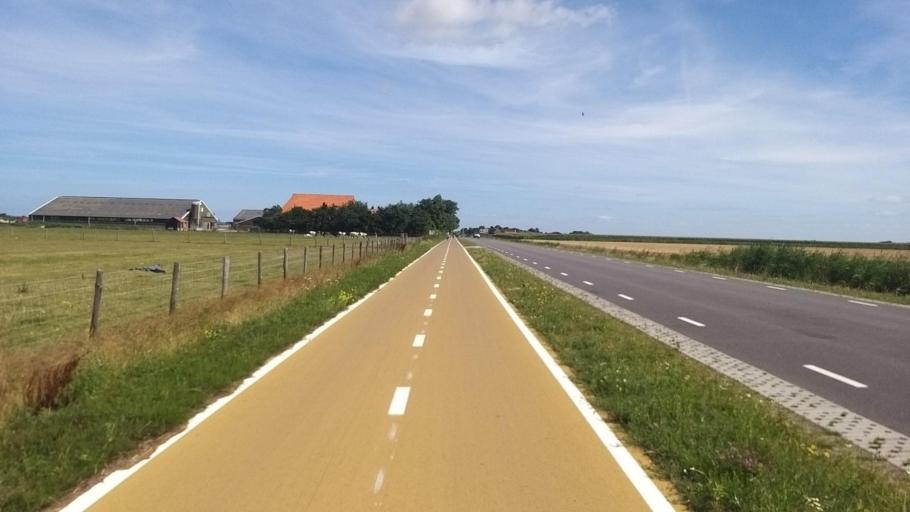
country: NL
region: North Holland
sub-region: Gemeente Texel
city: Den Burg
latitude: 53.1039
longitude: 4.8098
